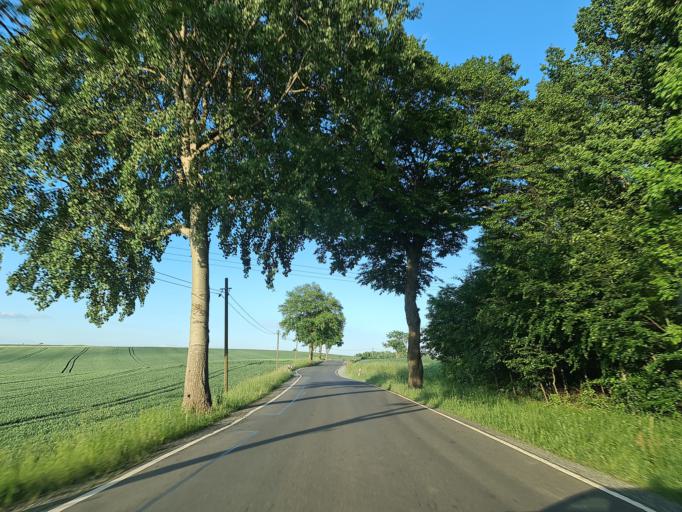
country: DE
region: Saxony
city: Reuth
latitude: 50.4649
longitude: 12.0093
